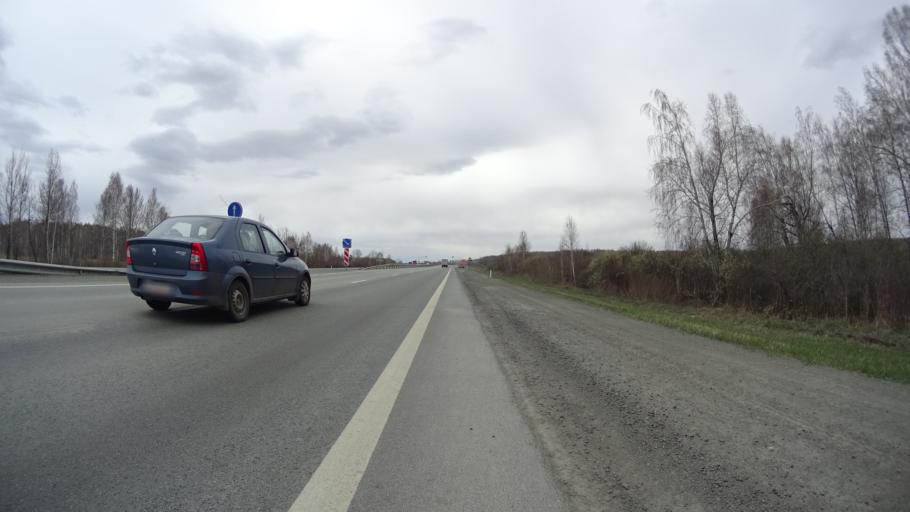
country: RU
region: Chelyabinsk
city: Yemanzhelinka
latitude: 54.8267
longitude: 61.3104
